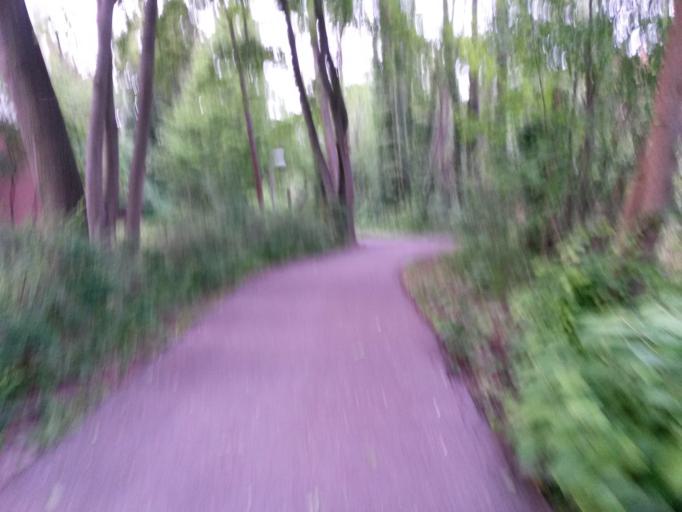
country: DE
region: Bavaria
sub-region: Regierungsbezirk Mittelfranken
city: Stein
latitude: 49.4134
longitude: 11.0189
